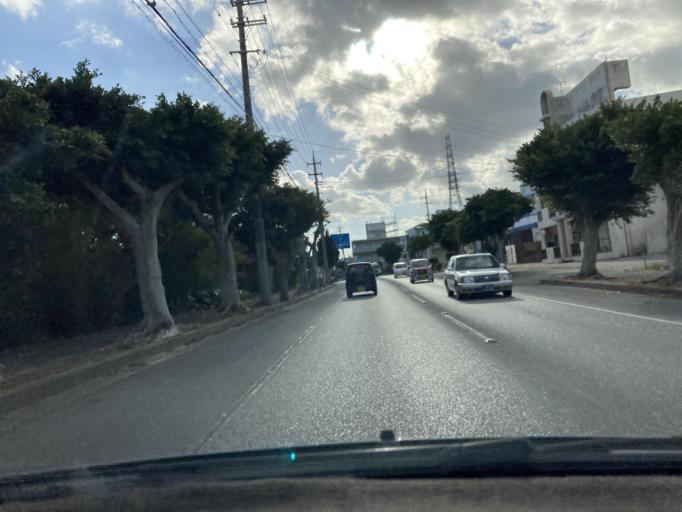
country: JP
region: Okinawa
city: Gushikawa
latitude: 26.3594
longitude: 127.8507
